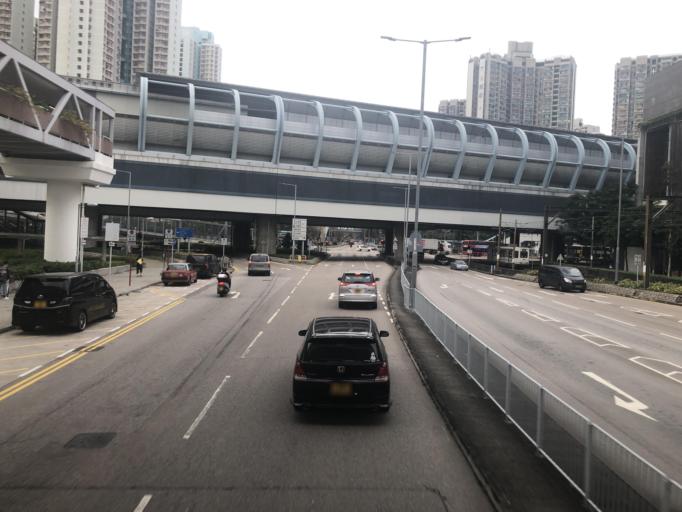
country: HK
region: Yuen Long
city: Yuen Long Kau Hui
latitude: 22.4466
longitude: 114.0044
